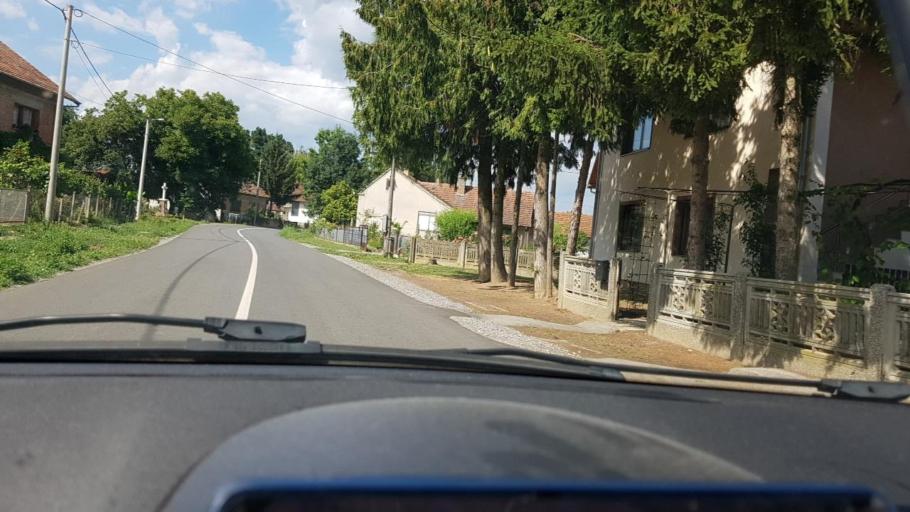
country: HR
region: Bjelovarsko-Bilogorska
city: Zdralovi
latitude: 45.8496
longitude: 16.9765
